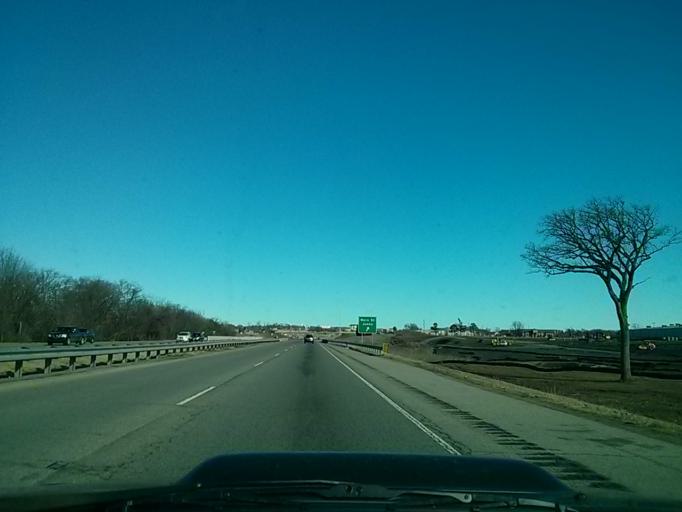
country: US
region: Oklahoma
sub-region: Tulsa County
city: Jenks
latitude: 36.0196
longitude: -96.0114
